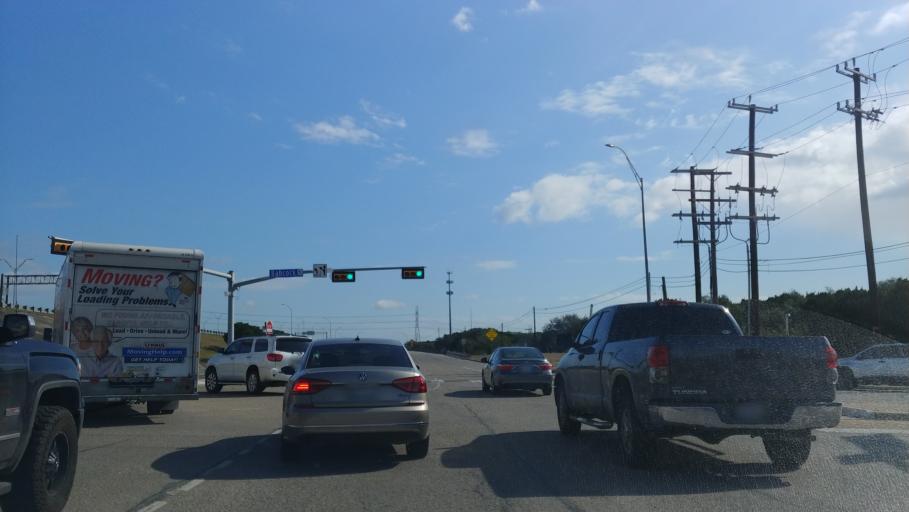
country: US
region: Texas
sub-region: Bexar County
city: Helotes
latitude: 29.5865
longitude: -98.6316
